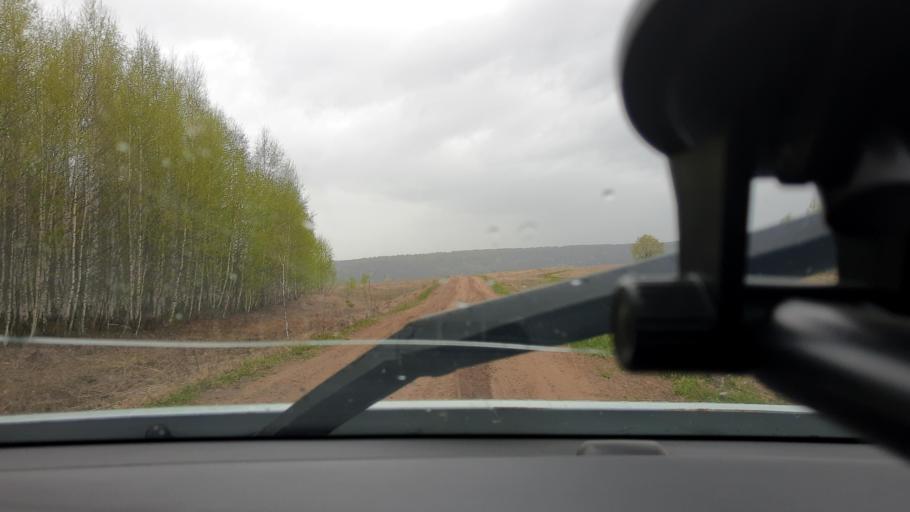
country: RU
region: Bashkortostan
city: Pavlovka
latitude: 55.4255
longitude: 56.3324
